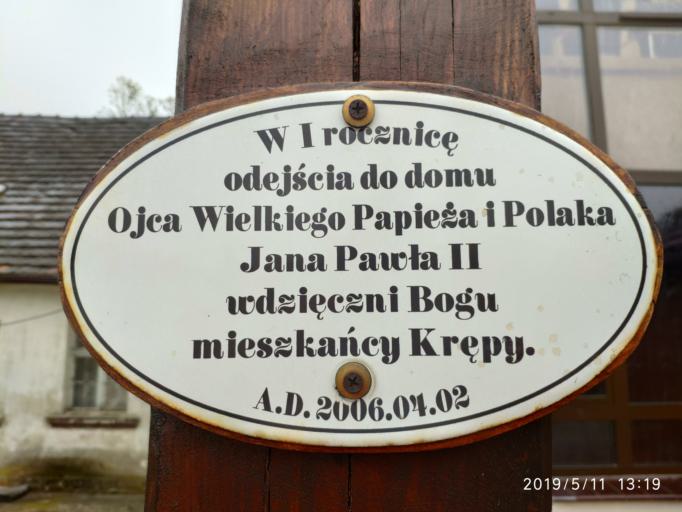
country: PL
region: Lubusz
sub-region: Zielona Gora
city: Zielona Gora
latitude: 51.9994
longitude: 15.5370
